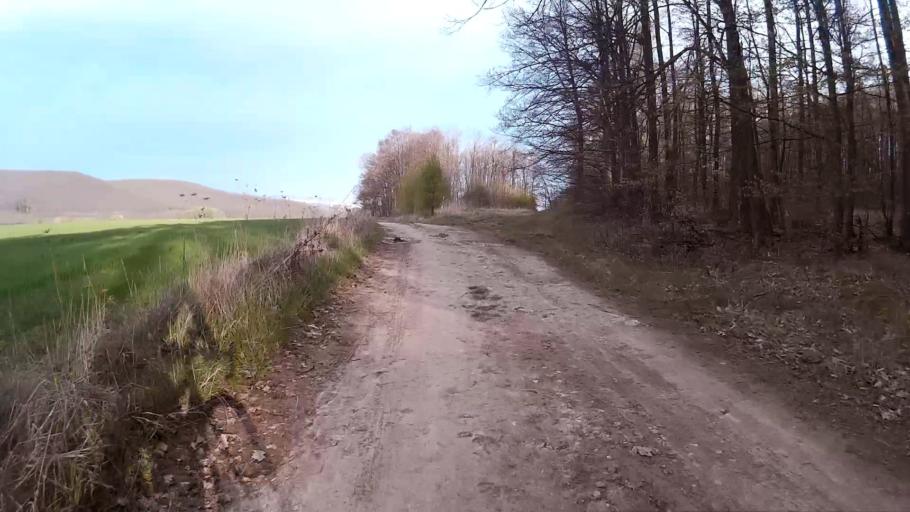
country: CZ
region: South Moravian
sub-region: Mesto Brno
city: Mokra Hora
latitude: 49.2455
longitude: 16.5405
